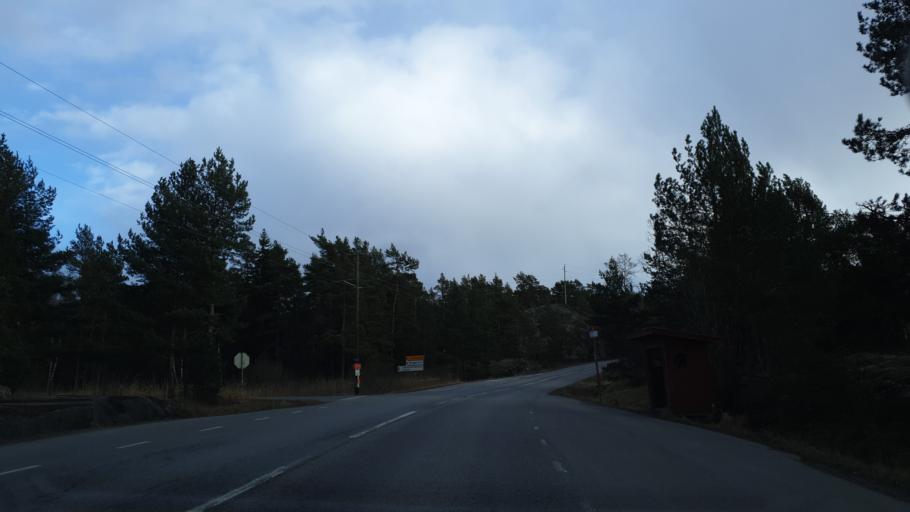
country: SE
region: Stockholm
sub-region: Varmdo Kommun
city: Holo
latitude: 59.3435
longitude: 18.7170
